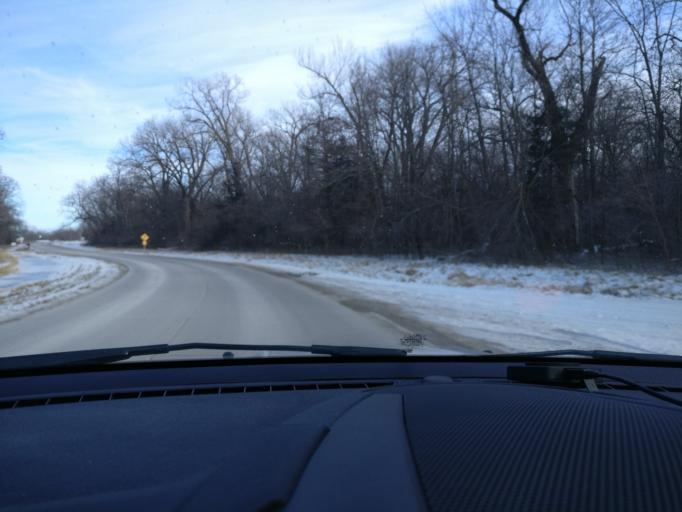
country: US
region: Nebraska
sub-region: Dodge County
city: Fremont
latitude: 41.4125
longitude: -96.5113
